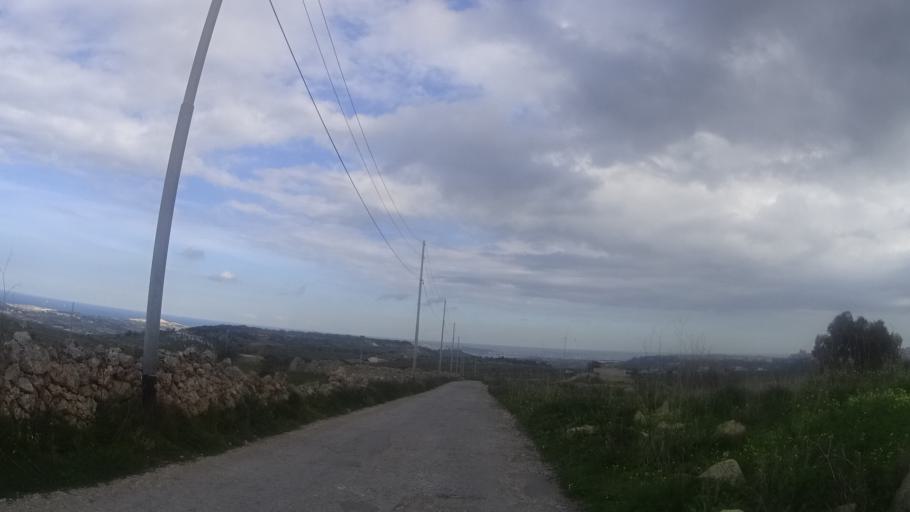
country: MT
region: L-Imgarr
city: Imgarr
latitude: 35.9009
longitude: 14.3721
